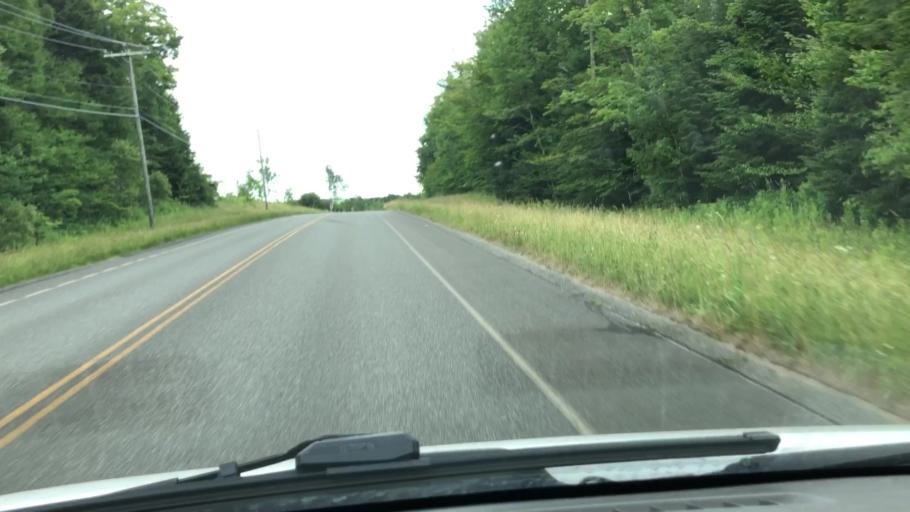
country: US
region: Massachusetts
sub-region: Berkshire County
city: Adams
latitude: 42.5383
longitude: -73.0553
